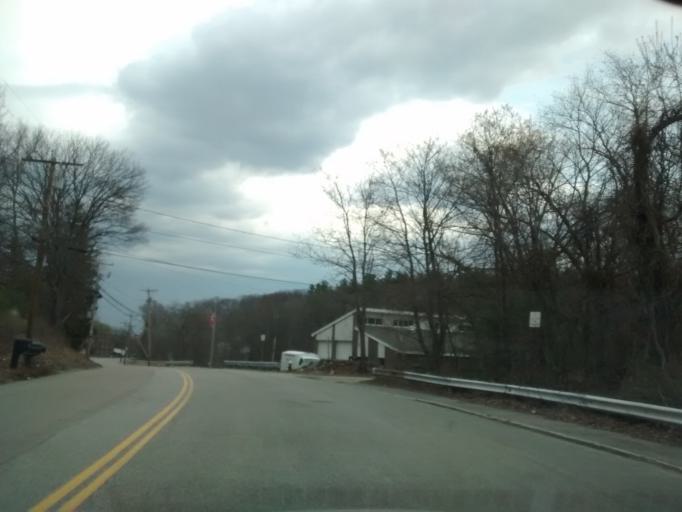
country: US
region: Massachusetts
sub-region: Worcester County
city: Sutton
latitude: 42.1704
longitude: -71.7824
